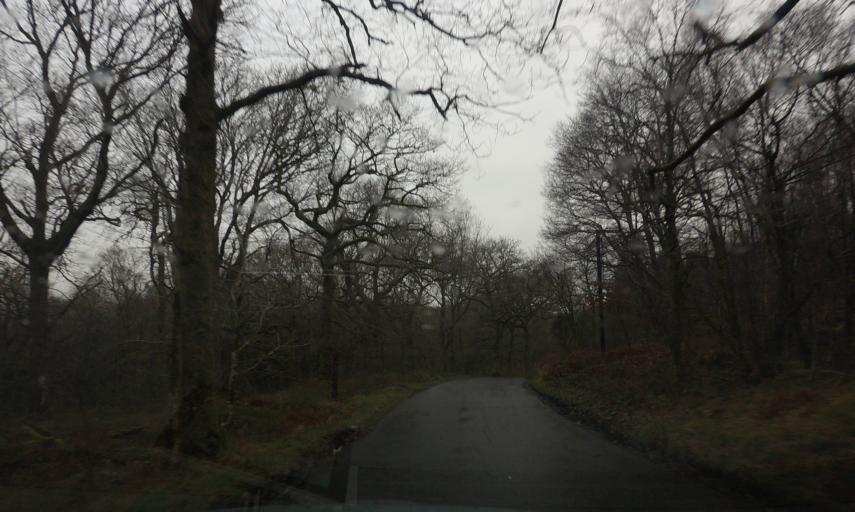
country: GB
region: Scotland
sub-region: West Dunbartonshire
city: Balloch
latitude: 56.1245
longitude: -4.6013
